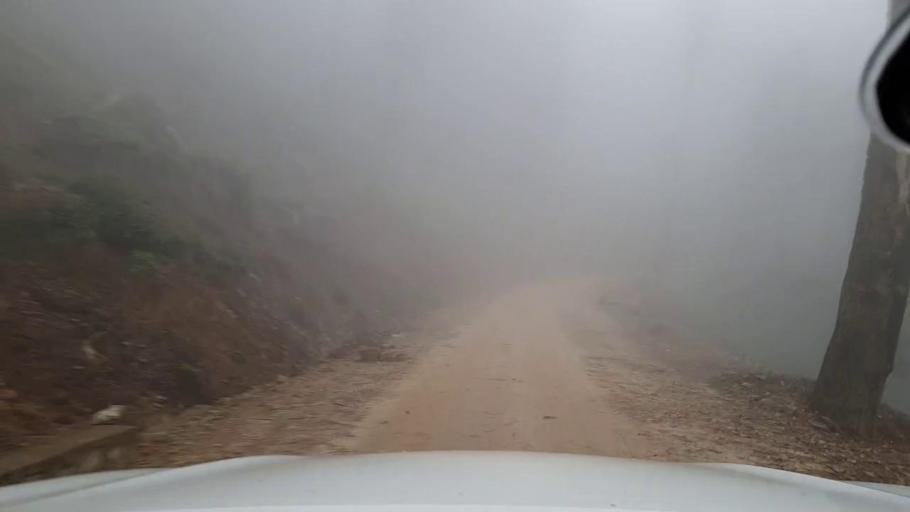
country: BI
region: Cibitoke
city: Cibitoke
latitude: -2.5967
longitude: 29.1947
